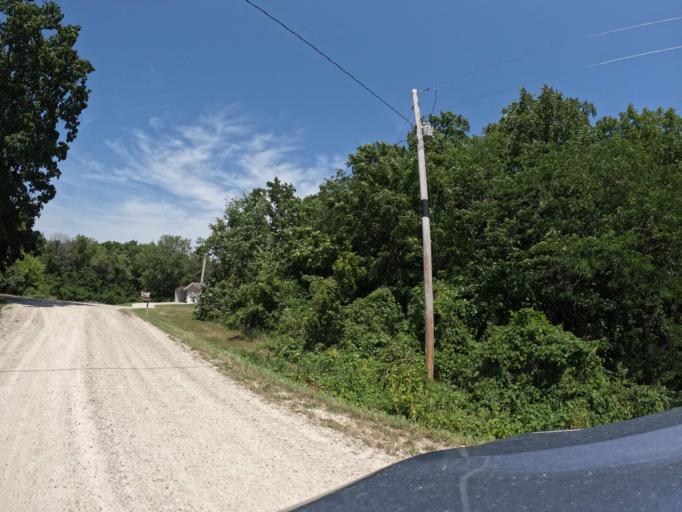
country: US
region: Iowa
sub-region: Henry County
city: Mount Pleasant
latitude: 40.9952
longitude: -91.6363
